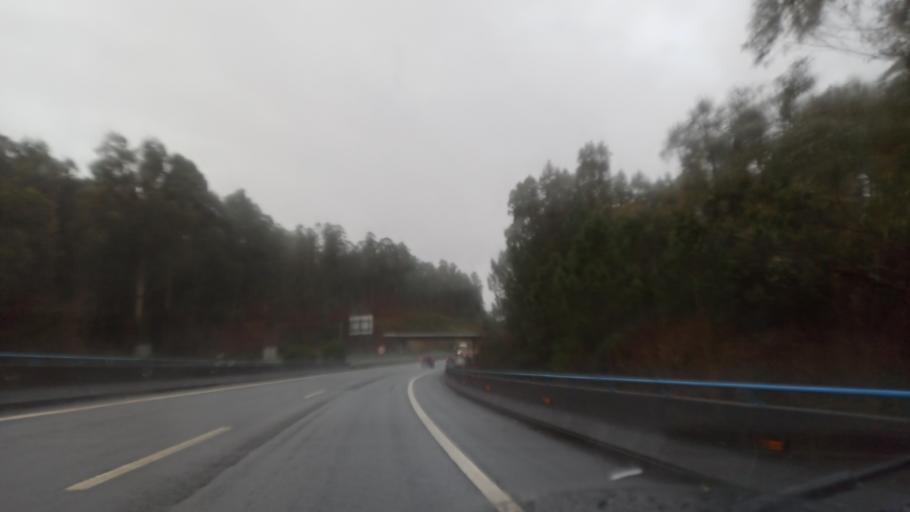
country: ES
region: Galicia
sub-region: Provincia da Coruna
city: Betanzos
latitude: 43.2594
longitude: -8.2147
